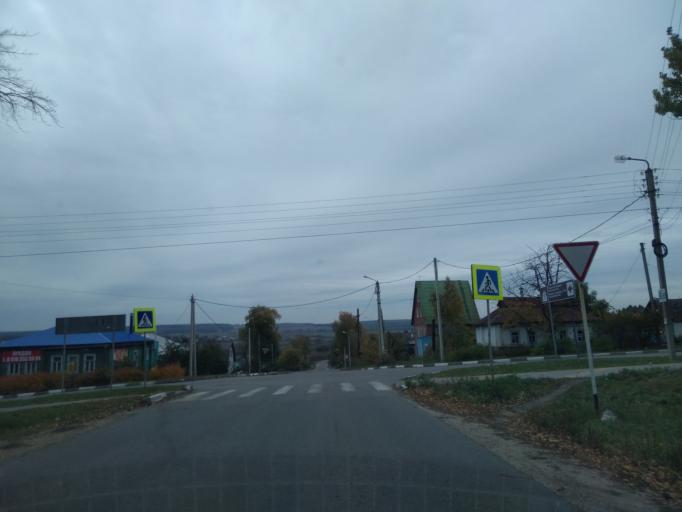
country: RU
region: Lipetsk
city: Zadonsk
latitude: 52.3838
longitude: 38.9187
